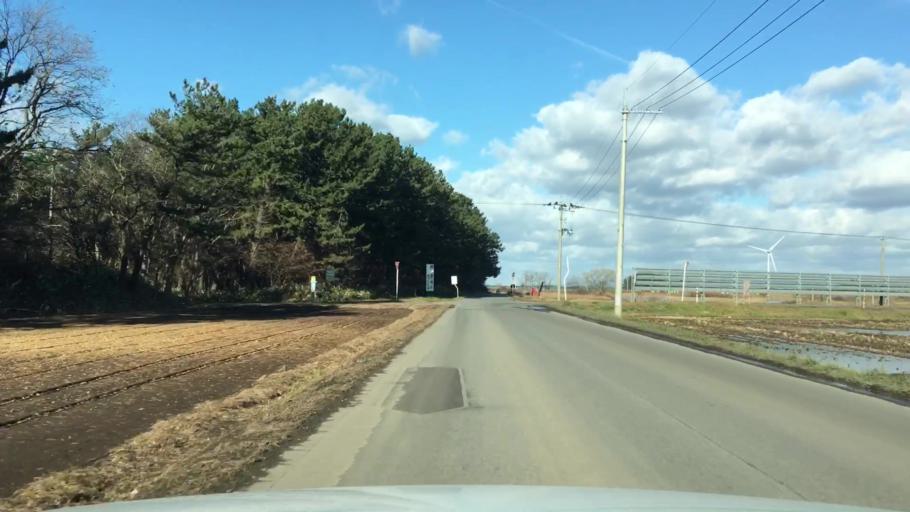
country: JP
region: Aomori
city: Shimokizukuri
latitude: 40.8485
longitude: 140.2999
